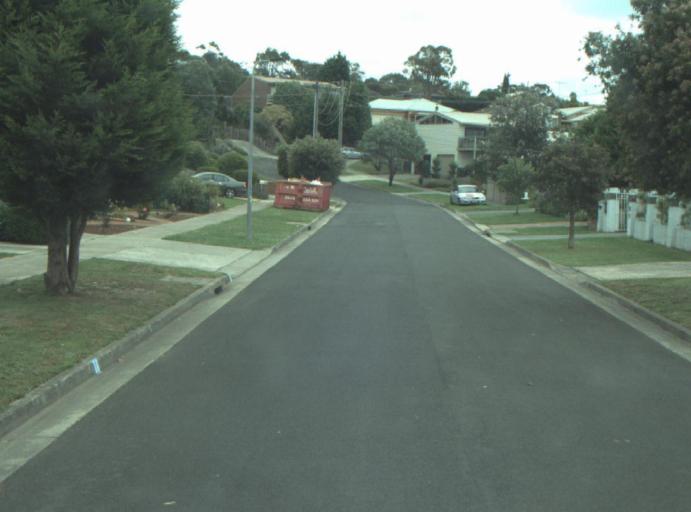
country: AU
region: Victoria
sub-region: Greater Geelong
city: Wandana Heights
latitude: -38.1953
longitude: 144.3245
